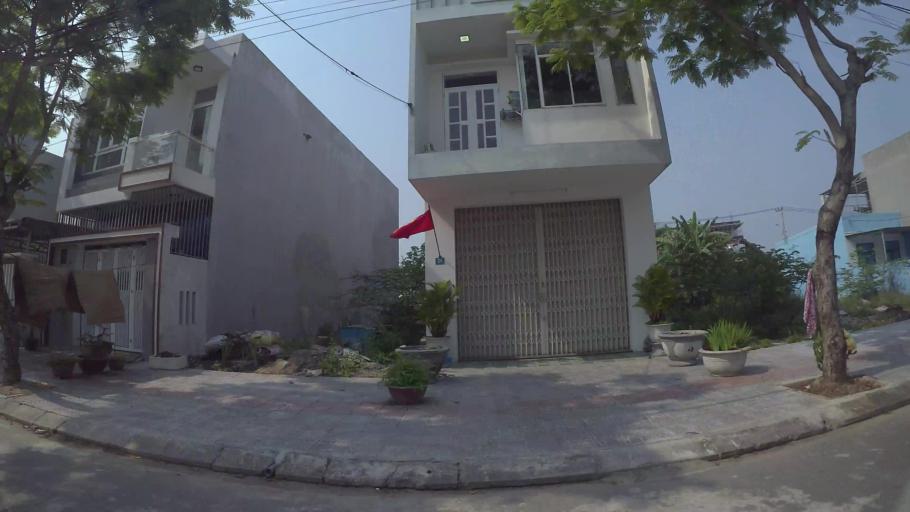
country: VN
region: Da Nang
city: Cam Le
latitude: 16.0040
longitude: 108.2216
